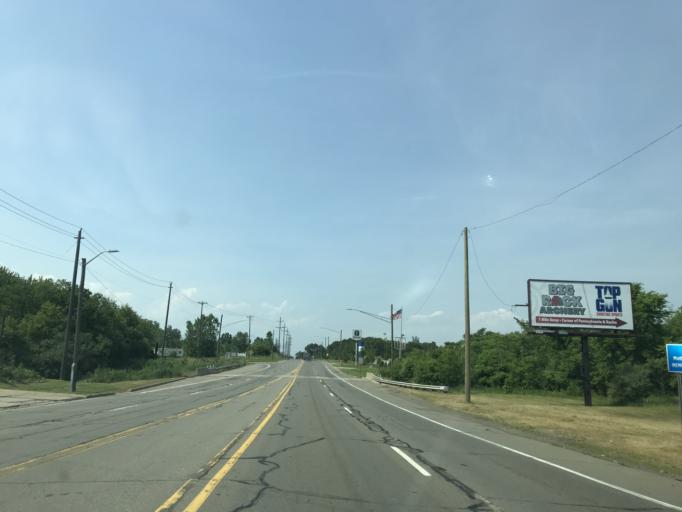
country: US
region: Michigan
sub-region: Wayne County
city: Woodhaven
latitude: 42.1844
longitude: -83.2673
